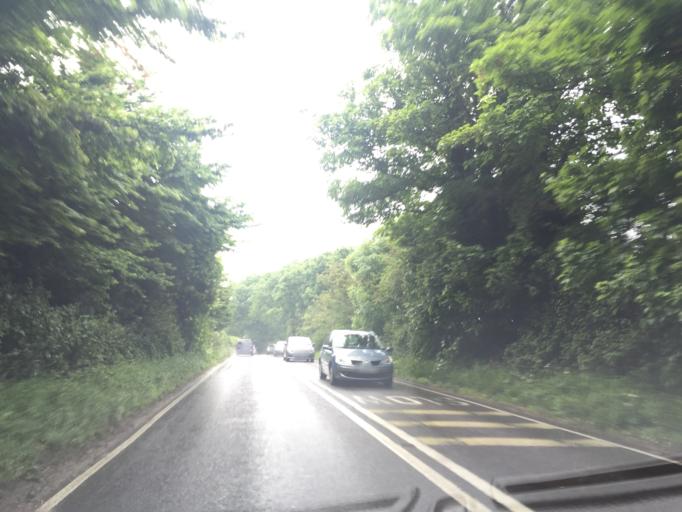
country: GB
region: England
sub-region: Dorset
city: Wareham
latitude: 50.6422
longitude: -2.0608
